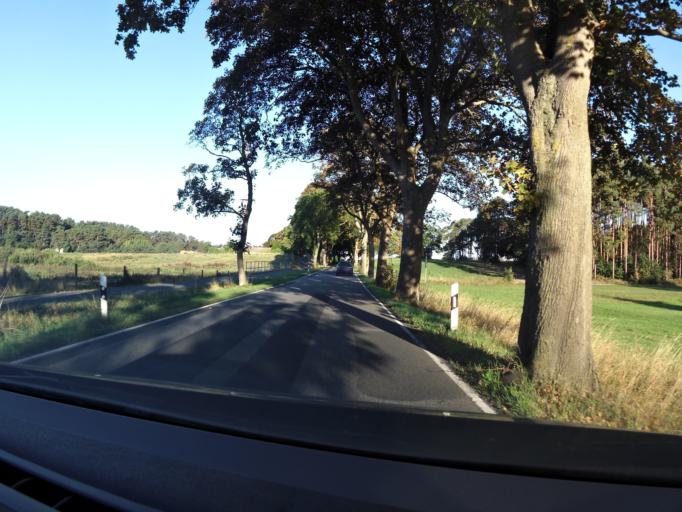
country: DE
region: Mecklenburg-Vorpommern
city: Seebad Bansin
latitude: 53.9398
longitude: 14.0526
